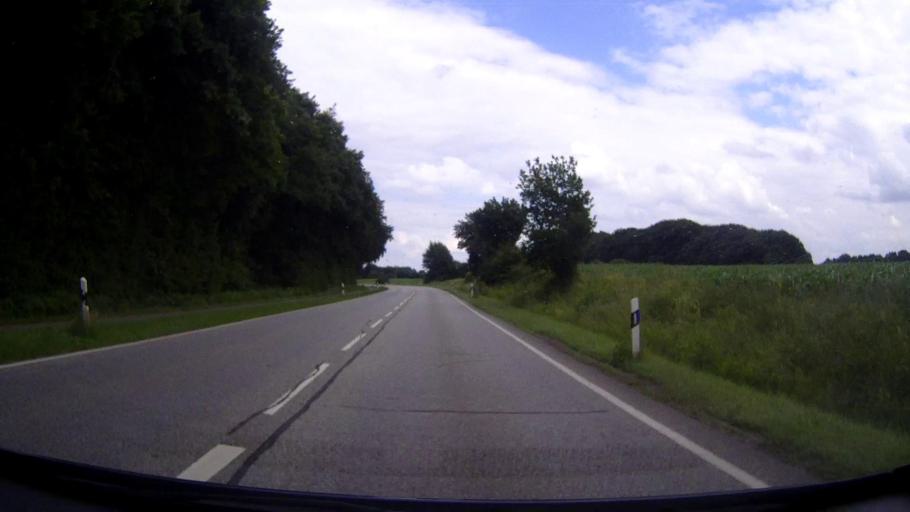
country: DE
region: Schleswig-Holstein
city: Aukrug
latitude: 54.0684
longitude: 9.7737
